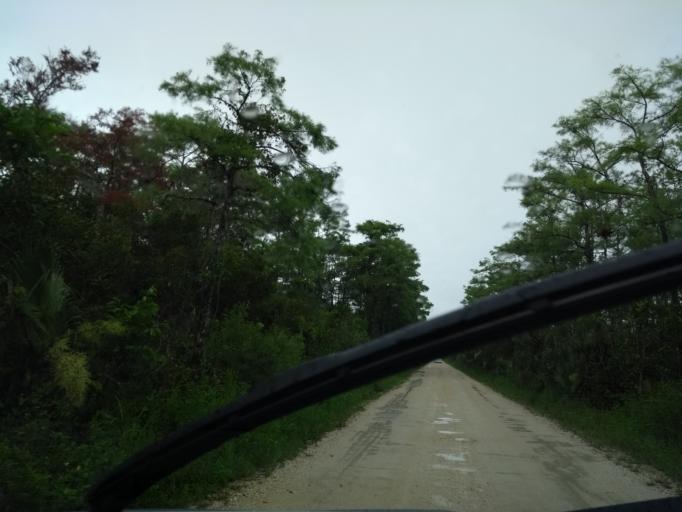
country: US
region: Florida
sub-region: Miami-Dade County
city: The Hammocks
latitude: 25.7602
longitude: -81.0409
